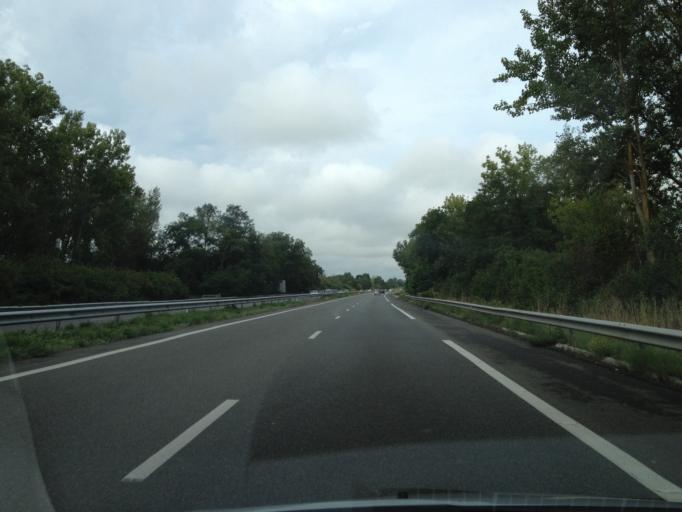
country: FR
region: Midi-Pyrenees
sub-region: Departement du Tarn-et-Garonne
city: Saint-Nicolas-de-la-Grave
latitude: 44.0415
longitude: 1.0496
